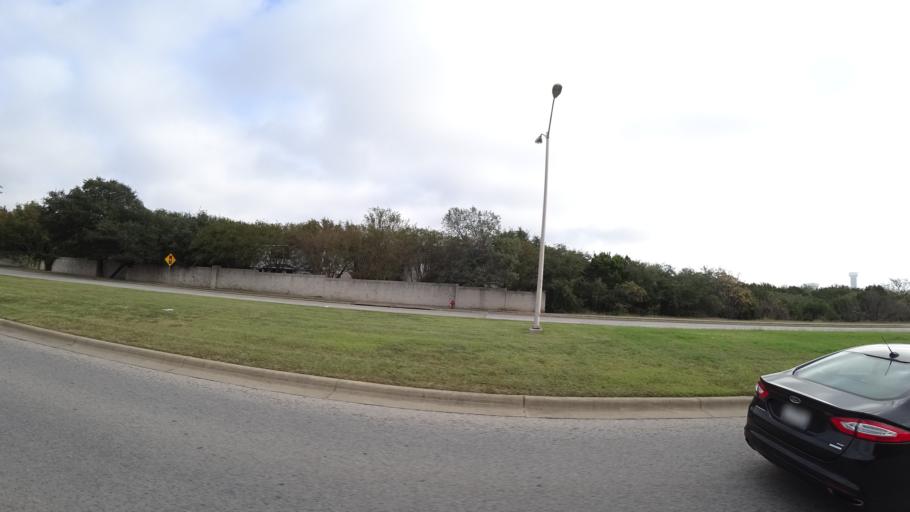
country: US
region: Texas
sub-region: Williamson County
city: Anderson Mill
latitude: 30.4623
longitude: -97.8430
